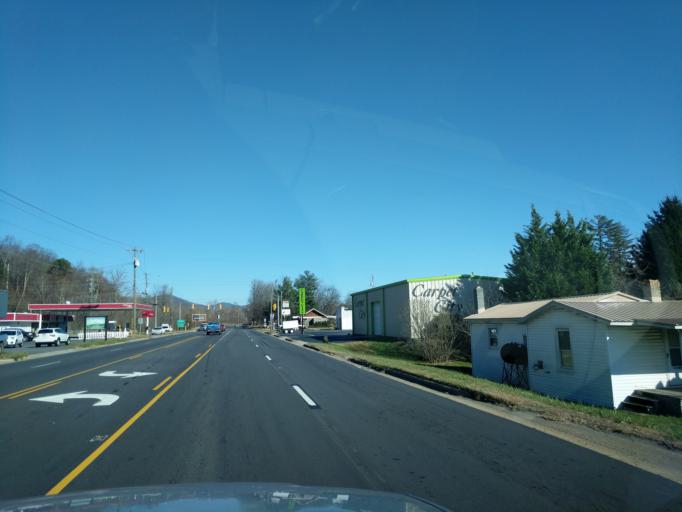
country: US
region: North Carolina
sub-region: Buncombe County
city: Swannanoa
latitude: 35.6013
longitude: -82.3992
